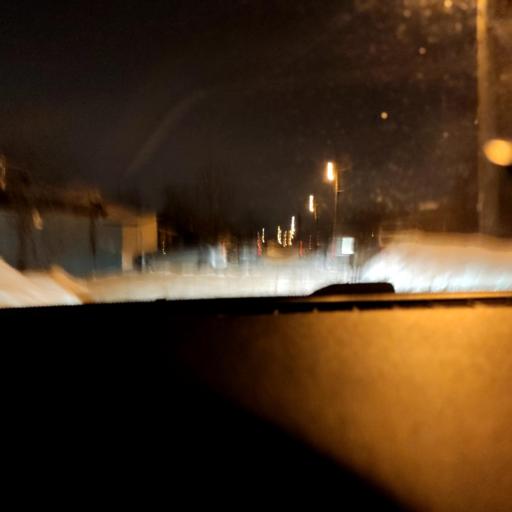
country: RU
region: Samara
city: Samara
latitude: 53.1379
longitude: 50.1310
